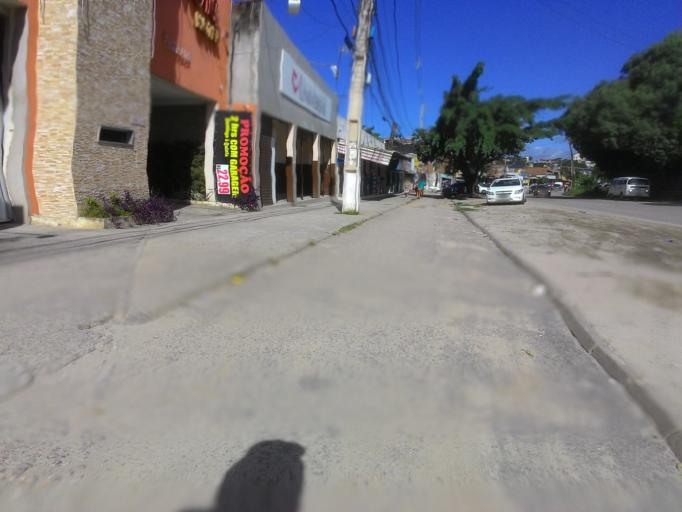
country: BR
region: Pernambuco
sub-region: Olinda
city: Olinda
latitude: -7.9810
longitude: -34.8567
